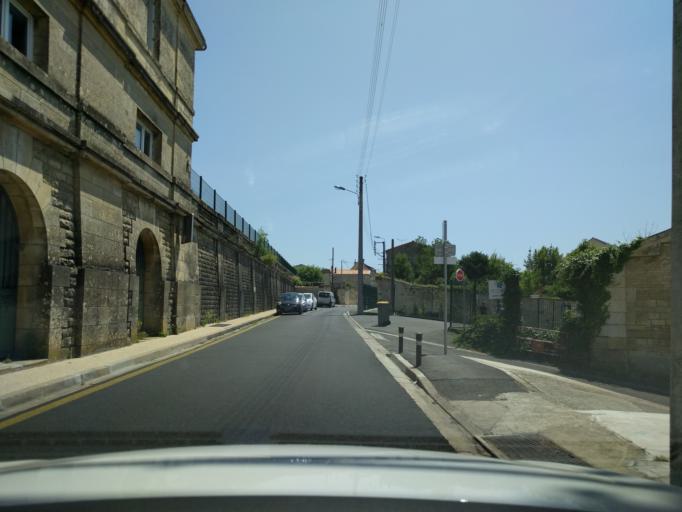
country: FR
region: Poitou-Charentes
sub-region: Departement des Deux-Sevres
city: Niort
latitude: 46.3329
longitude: -0.4608
